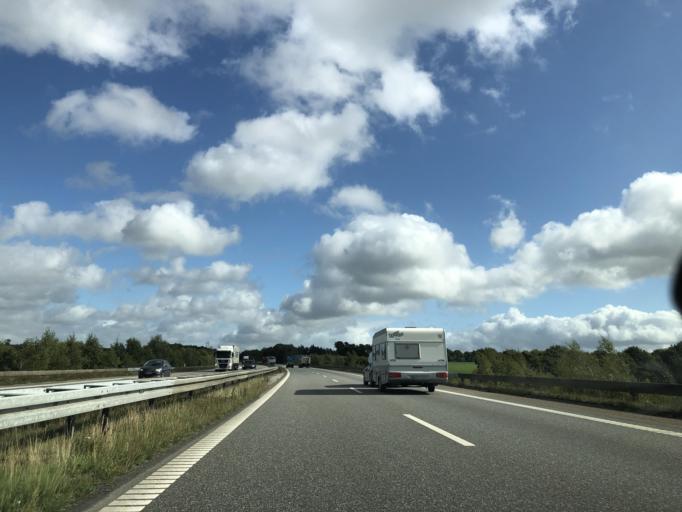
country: DK
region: North Denmark
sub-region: Mariagerfjord Kommune
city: Hobro
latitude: 56.5813
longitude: 9.7998
